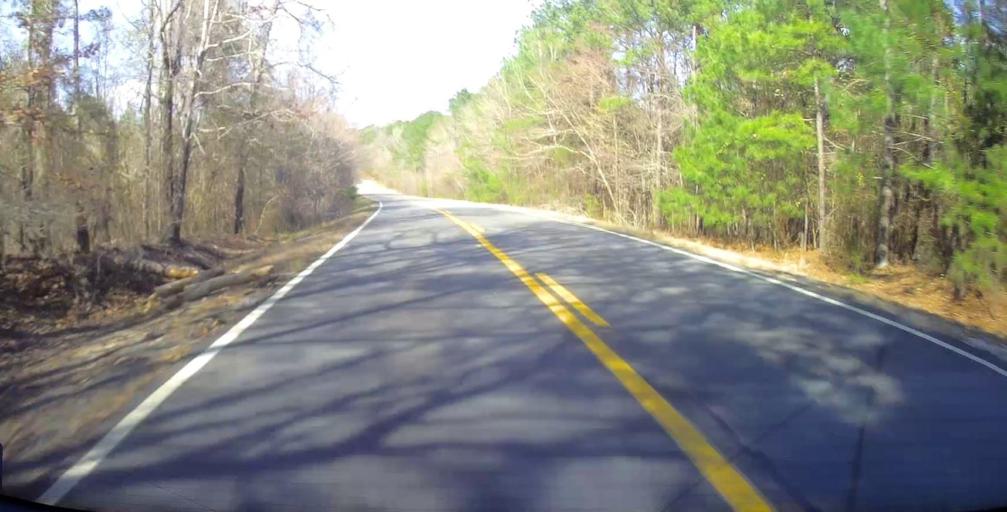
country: US
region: Georgia
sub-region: Twiggs County
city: Jeffersonville
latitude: 32.7479
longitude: -83.3436
